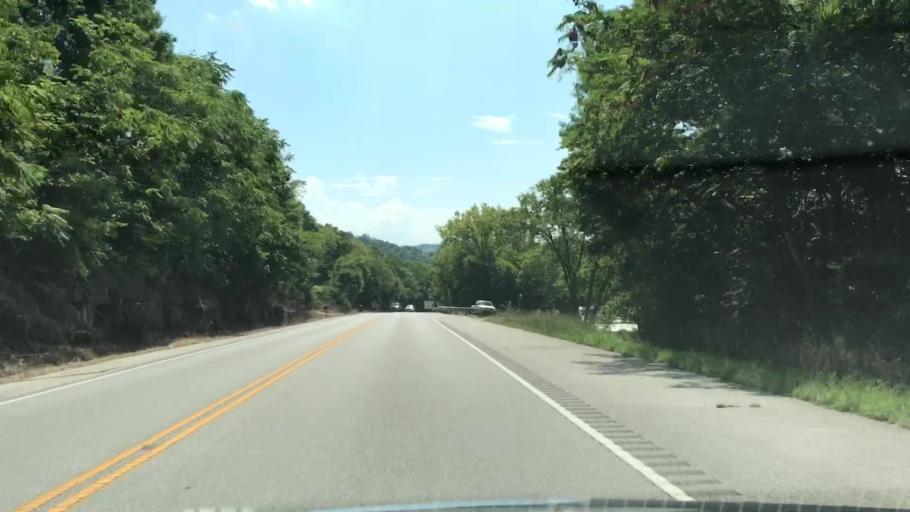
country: US
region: Tennessee
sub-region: Smith County
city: Carthage
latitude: 36.3214
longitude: -86.0157
